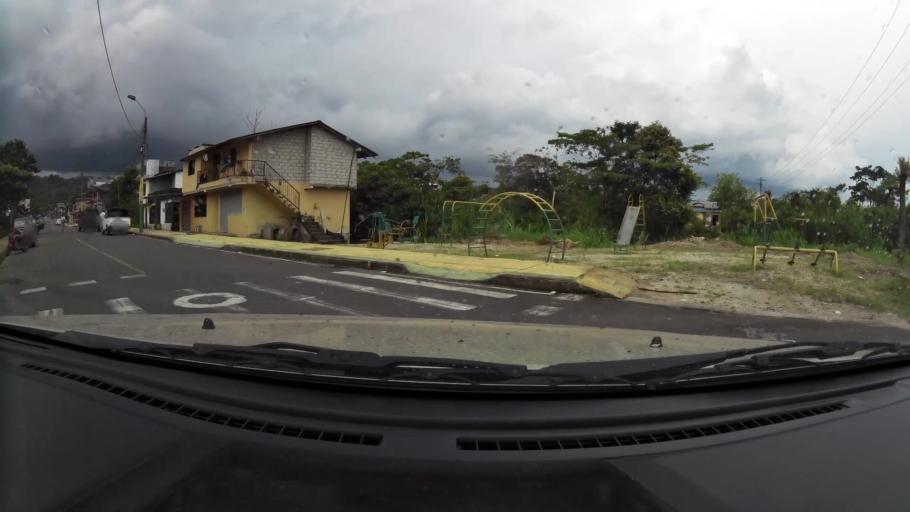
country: EC
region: Pastaza
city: Puyo
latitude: -1.4939
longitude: -78.0085
